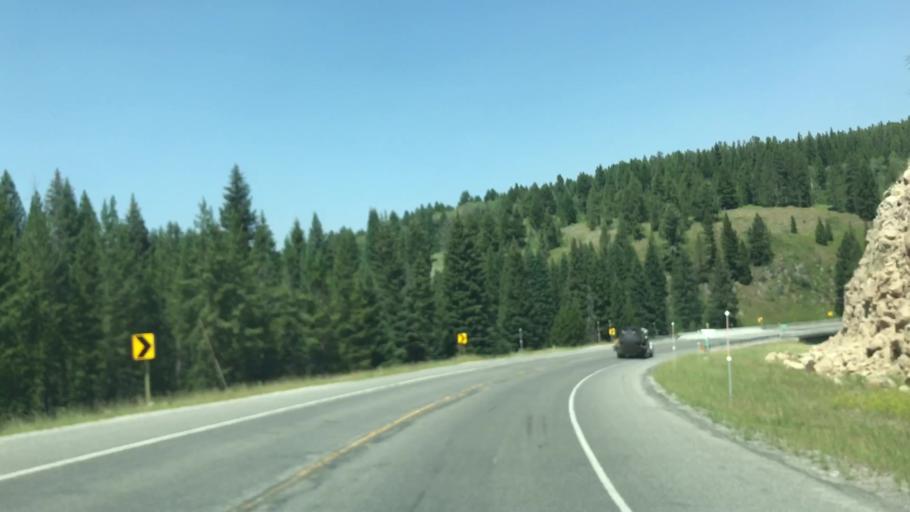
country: US
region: Montana
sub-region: Gallatin County
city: West Yellowstone
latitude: 44.8009
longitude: -111.1080
